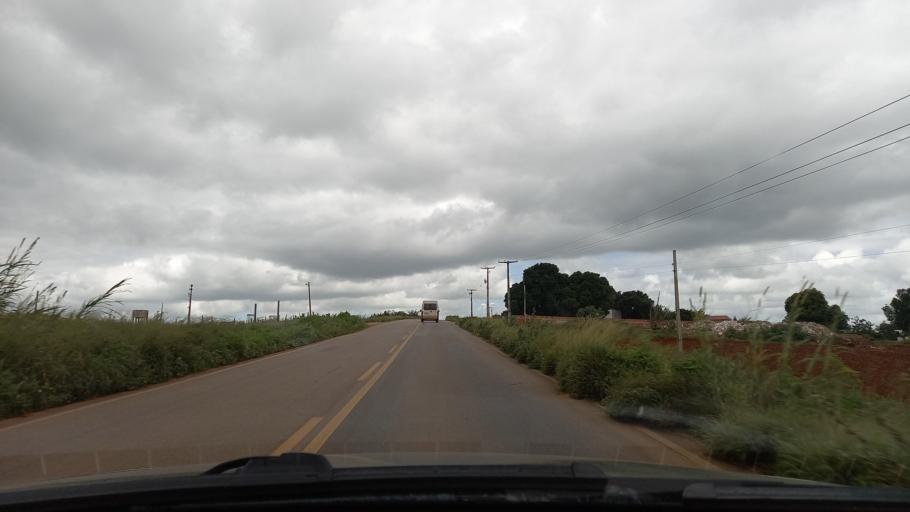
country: BR
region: Sergipe
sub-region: Caninde De Sao Francisco
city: Caninde de Sao Francisco
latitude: -9.6756
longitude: -37.8022
